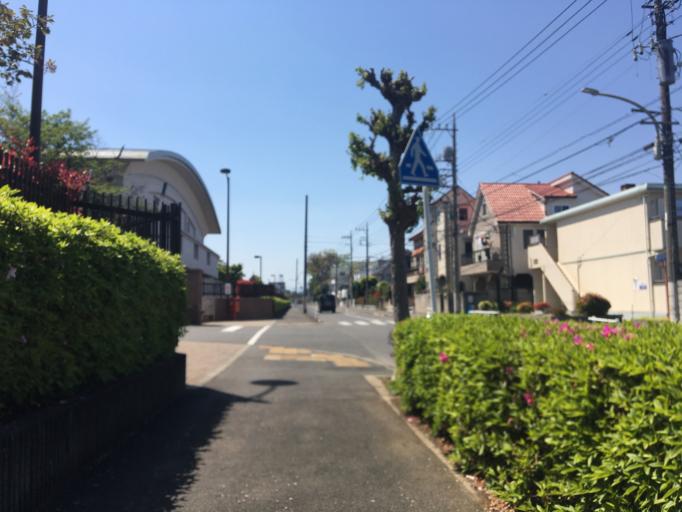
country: JP
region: Tokyo
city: Kokubunji
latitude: 35.7217
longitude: 139.4844
